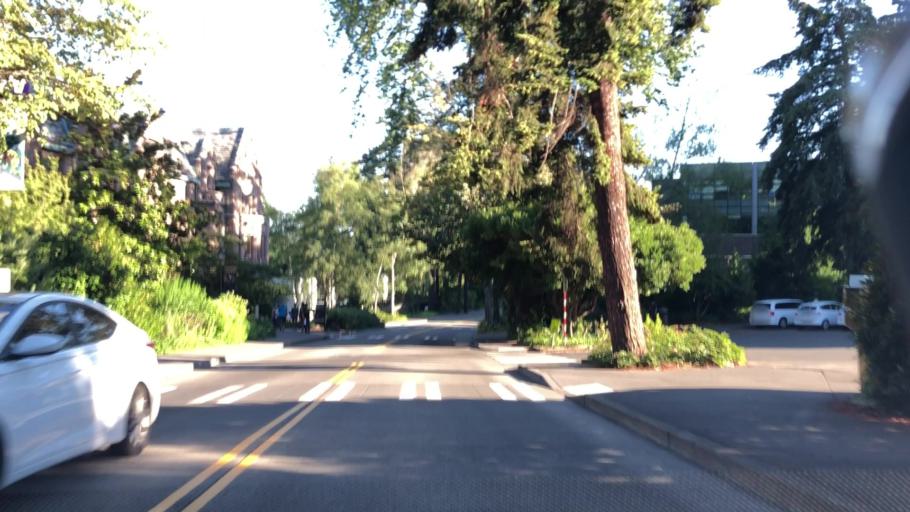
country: US
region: Washington
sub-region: King County
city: Seattle
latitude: 47.6567
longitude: -122.3048
